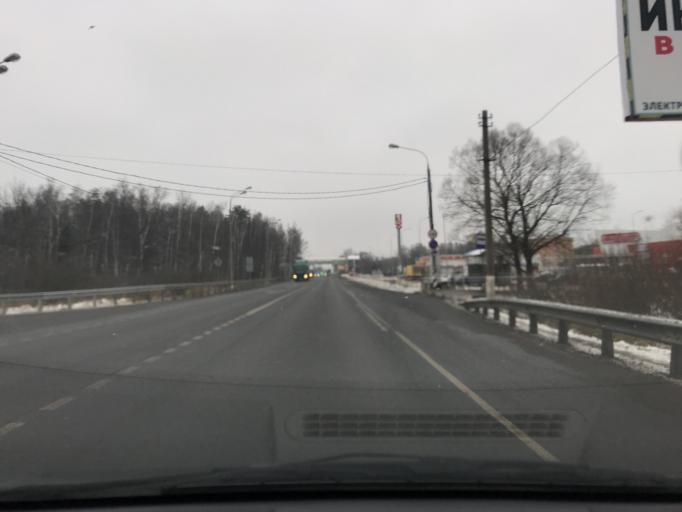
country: RU
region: Moskovskaya
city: Elektrostal'
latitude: 55.8033
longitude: 38.4281
